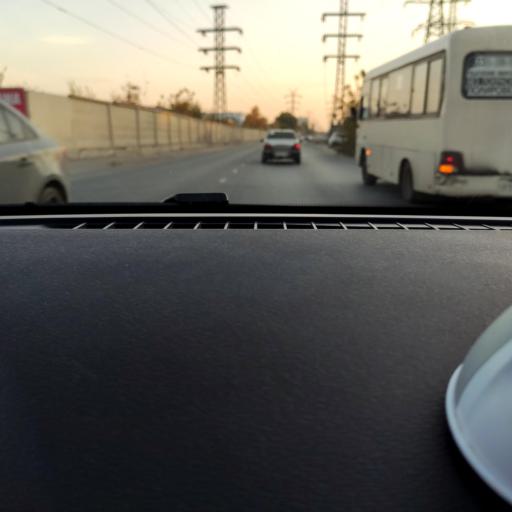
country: RU
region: Samara
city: Petra-Dubrava
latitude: 53.2452
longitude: 50.2920
